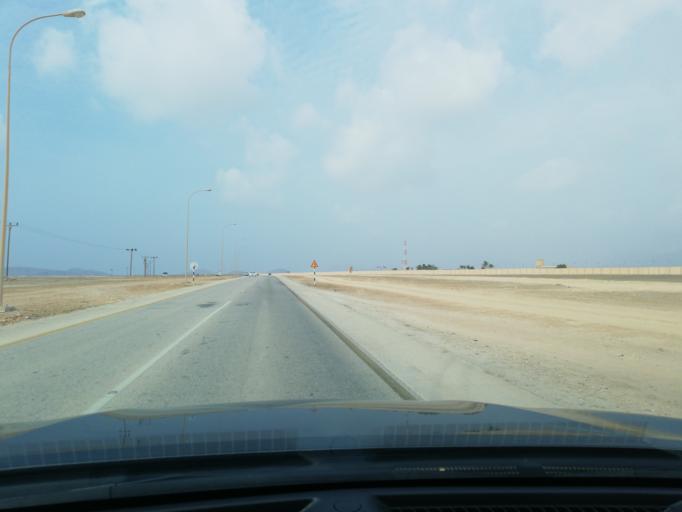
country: OM
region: Zufar
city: Salalah
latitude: 16.9423
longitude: 53.8471
